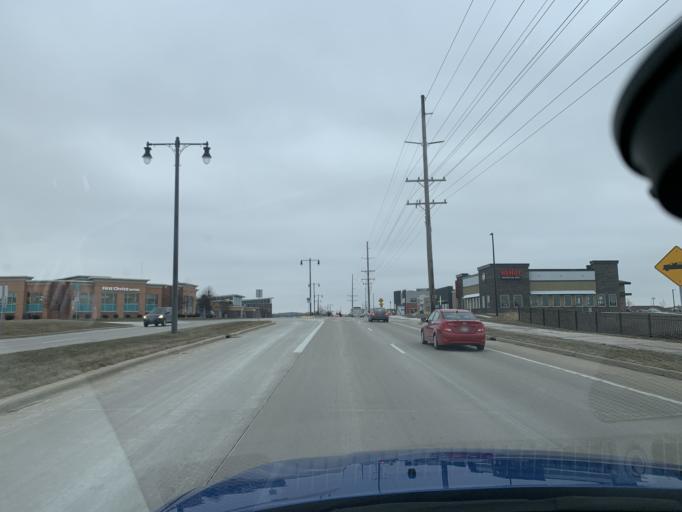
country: US
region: Wisconsin
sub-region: Dane County
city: Sun Prairie
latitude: 43.1786
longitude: -89.2649
